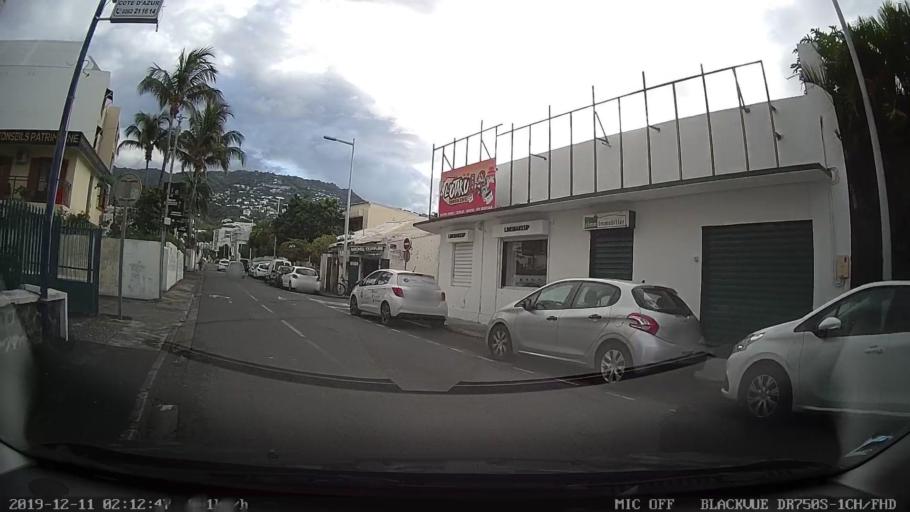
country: RE
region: Reunion
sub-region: Reunion
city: Saint-Denis
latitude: -20.8869
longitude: 55.4540
